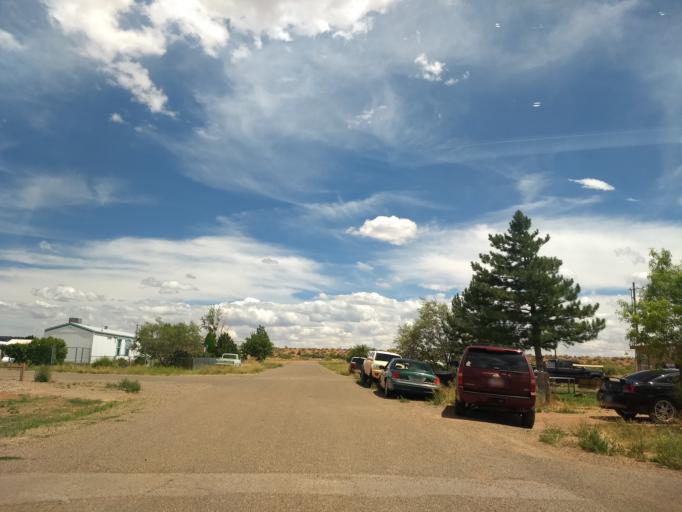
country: US
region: Arizona
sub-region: Coconino County
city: Fredonia
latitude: 36.9595
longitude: -112.5242
